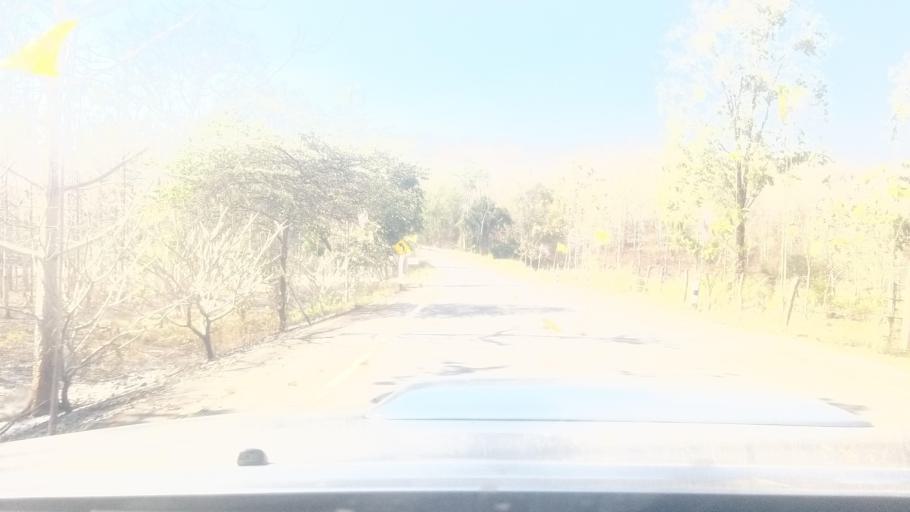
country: TH
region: Phrae
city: Nong Muang Khai
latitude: 18.2917
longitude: 100.0634
